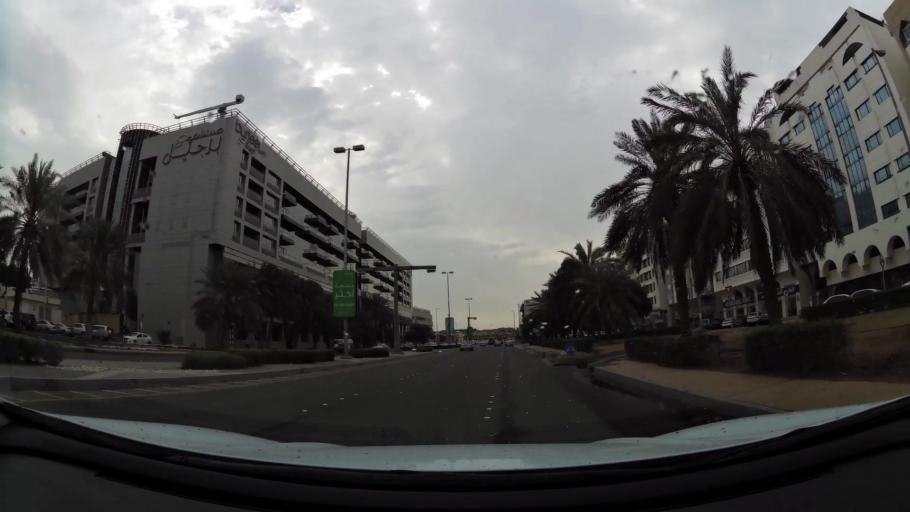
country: AE
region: Abu Dhabi
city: Abu Dhabi
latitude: 24.4795
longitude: 54.3798
